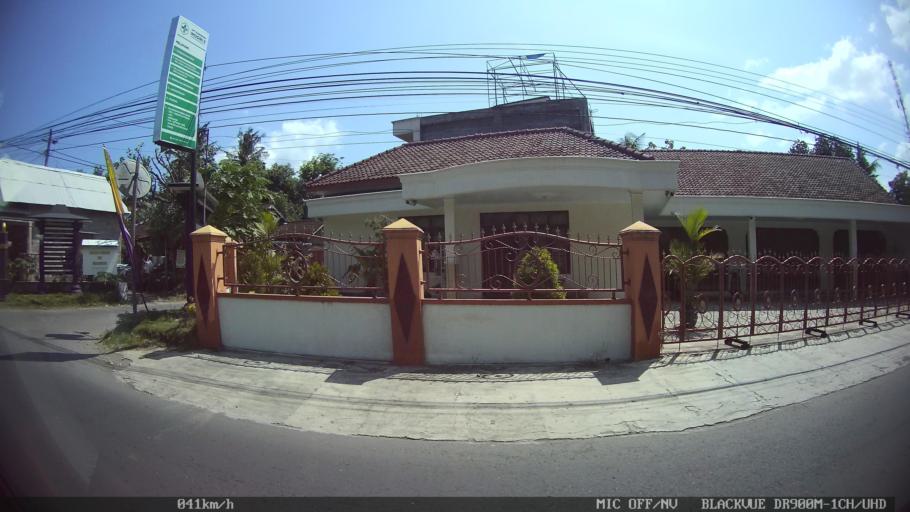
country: ID
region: Daerah Istimewa Yogyakarta
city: Pundong
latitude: -7.9443
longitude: 110.3743
